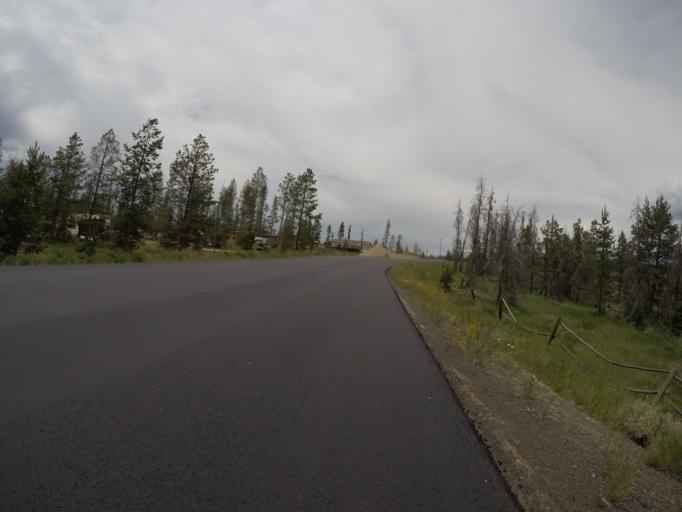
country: US
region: Colorado
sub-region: Grand County
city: Granby
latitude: 39.9987
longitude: -105.9012
